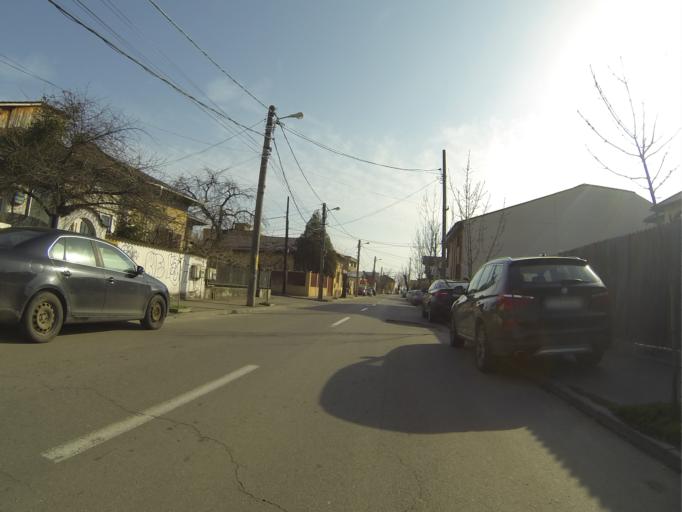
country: RO
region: Dolj
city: Craiova
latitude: 44.3115
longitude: 23.8113
